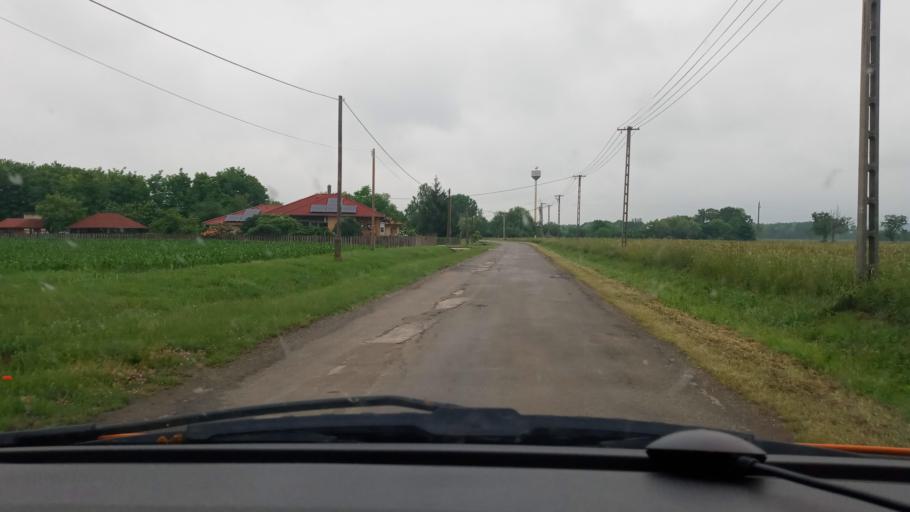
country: HU
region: Baranya
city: Szentlorinc
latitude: 46.0487
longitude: 17.9682
